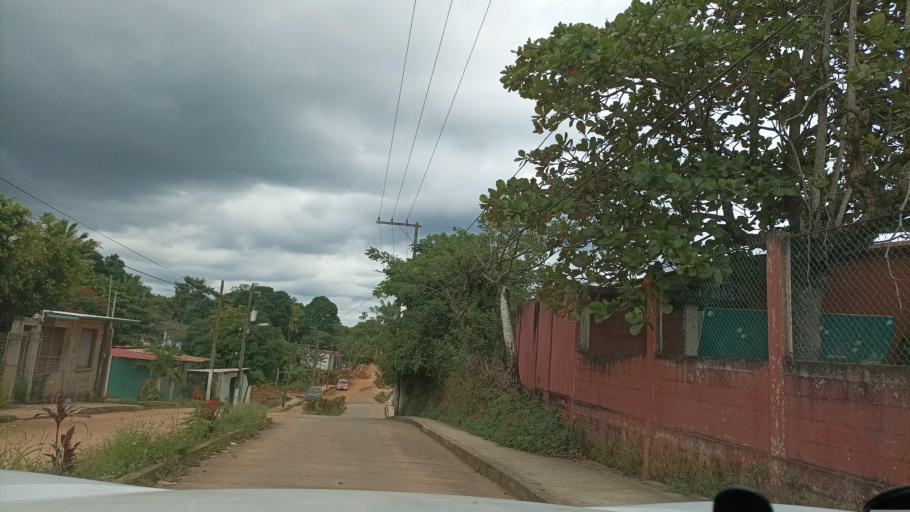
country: MX
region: Veracruz
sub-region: Soconusco
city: Colonia Lealtad
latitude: 17.9621
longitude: -94.8976
